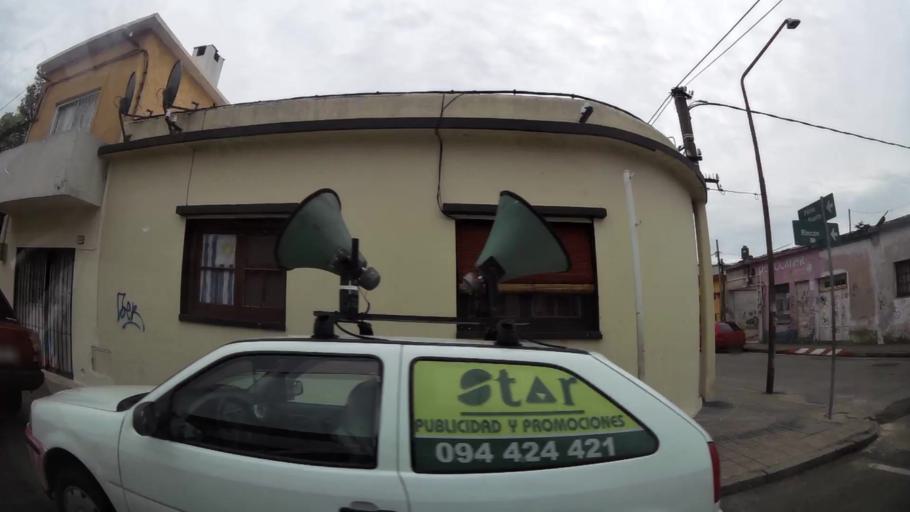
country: UY
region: Maldonado
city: Maldonado
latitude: -34.9102
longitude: -54.9555
